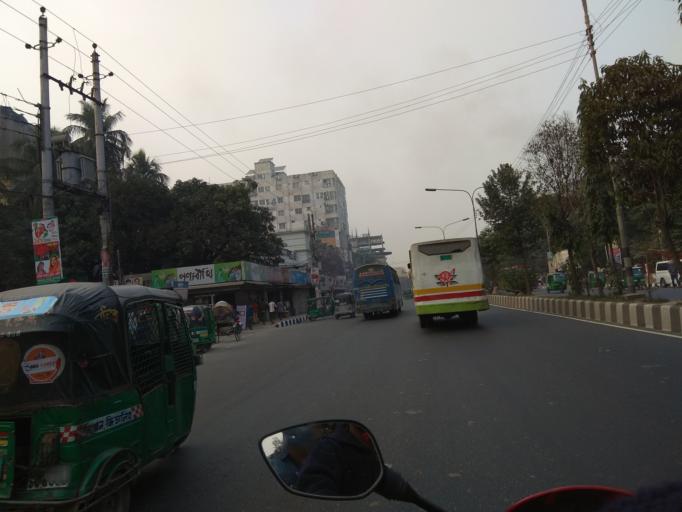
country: BD
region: Dhaka
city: Azimpur
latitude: 23.7699
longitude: 90.3685
